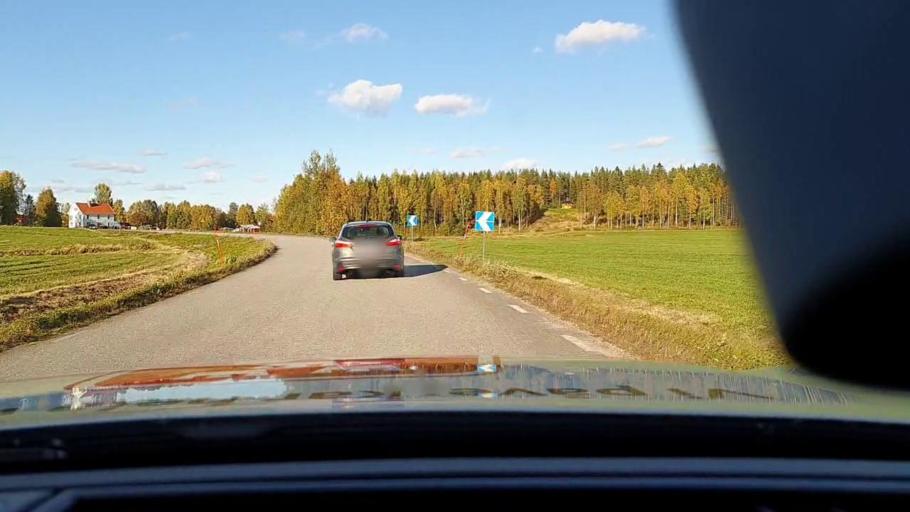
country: SE
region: Norrbotten
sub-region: Pitea Kommun
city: Norrfjarden
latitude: 65.5133
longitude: 21.4949
